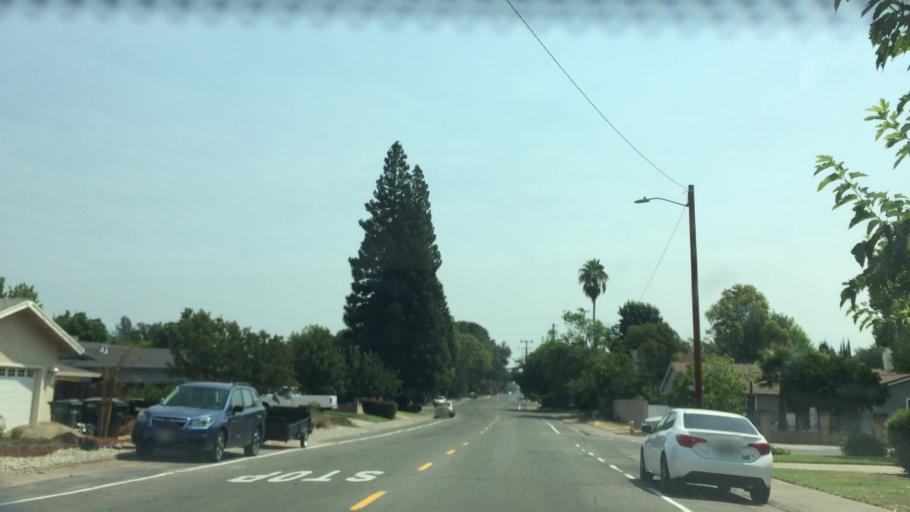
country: US
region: California
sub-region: Sacramento County
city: Arden-Arcade
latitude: 38.6320
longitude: -121.3668
